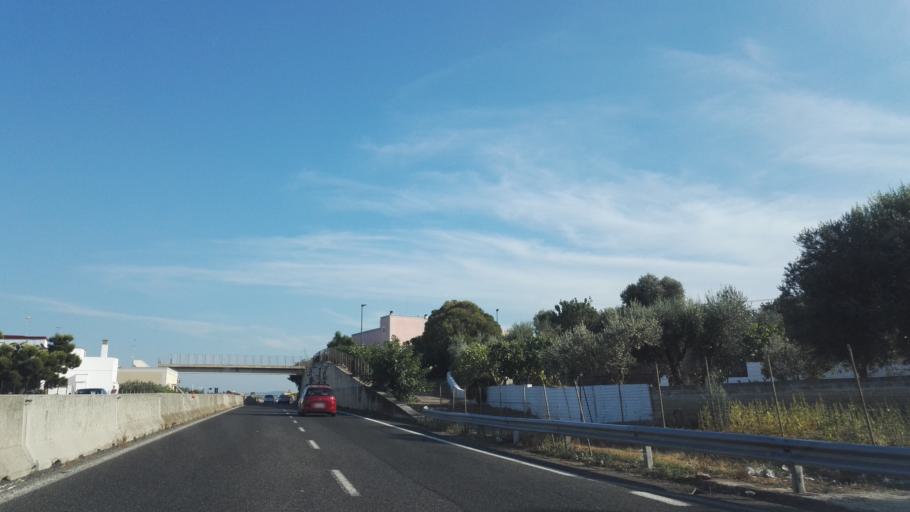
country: IT
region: Apulia
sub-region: Provincia di Brindisi
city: Fasano
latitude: 40.8919
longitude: 17.3322
